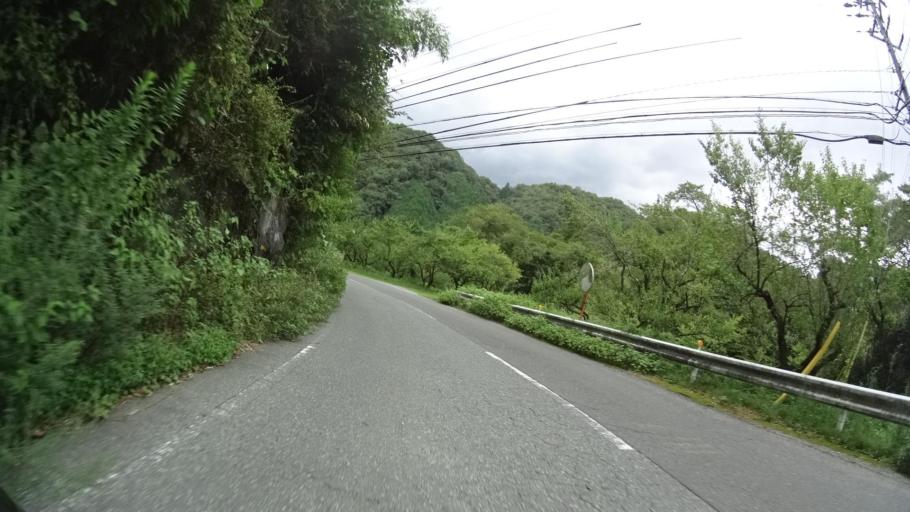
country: JP
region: Mie
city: Nabari
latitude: 34.7068
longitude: 136.0201
